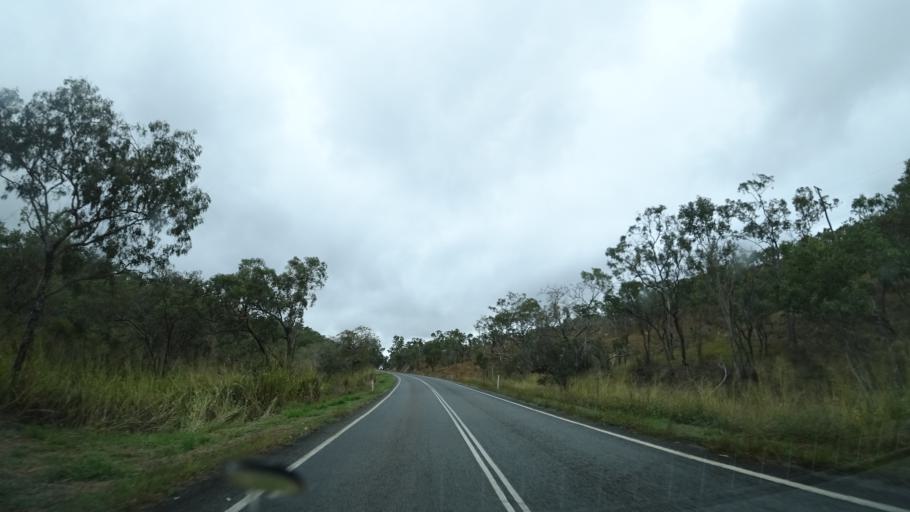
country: AU
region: Queensland
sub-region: Cairns
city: Port Douglas
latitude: -16.7024
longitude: 145.3469
